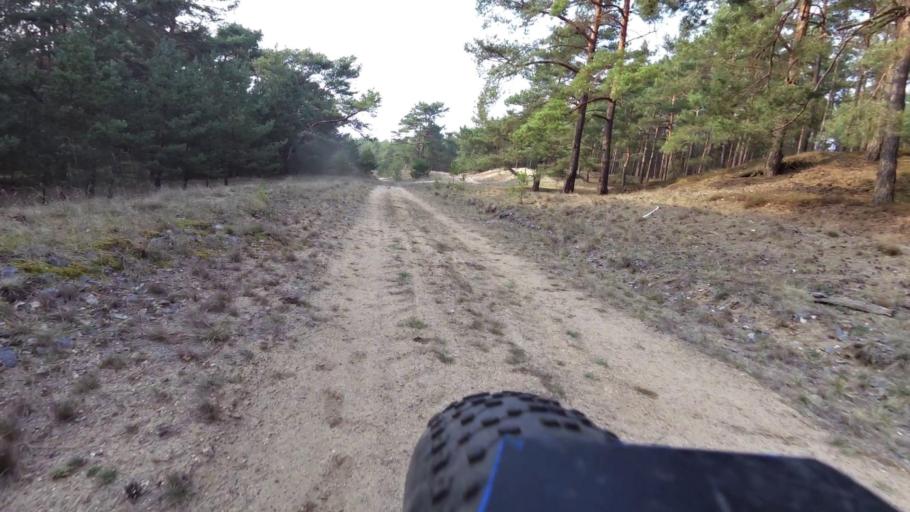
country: PL
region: Lubusz
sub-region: Powiat slubicki
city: Cybinka
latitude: 52.2478
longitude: 14.7517
